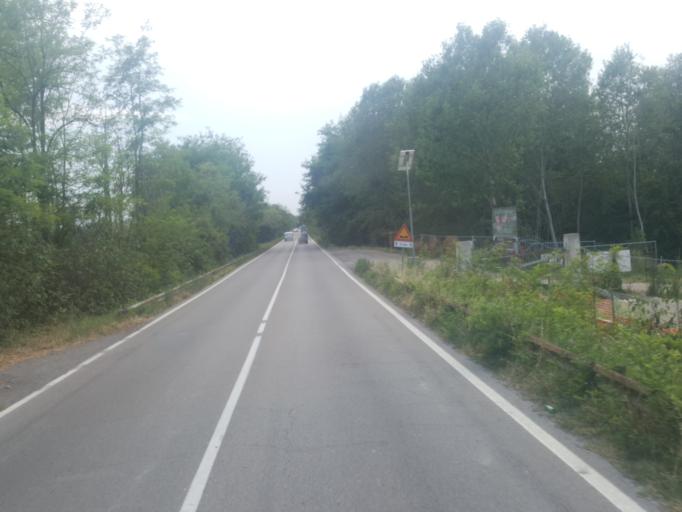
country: IT
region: Emilia-Romagna
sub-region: Provincia di Modena
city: Gaggio
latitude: 44.6226
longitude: 10.9968
